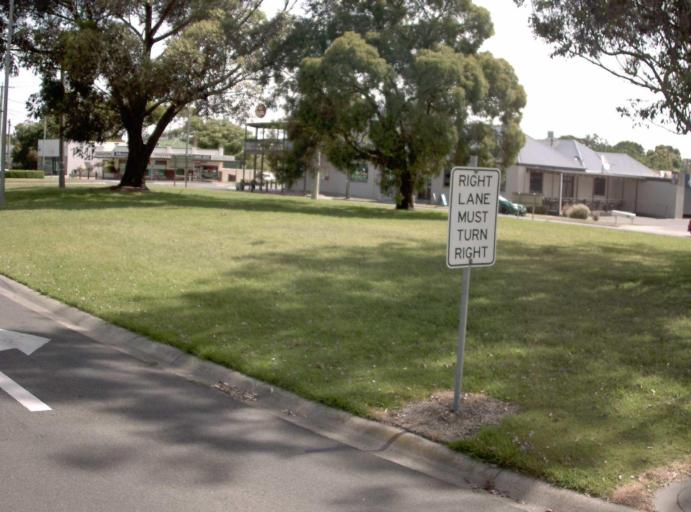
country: AU
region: Victoria
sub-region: Wellington
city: Heyfield
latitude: -38.1510
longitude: 146.7900
